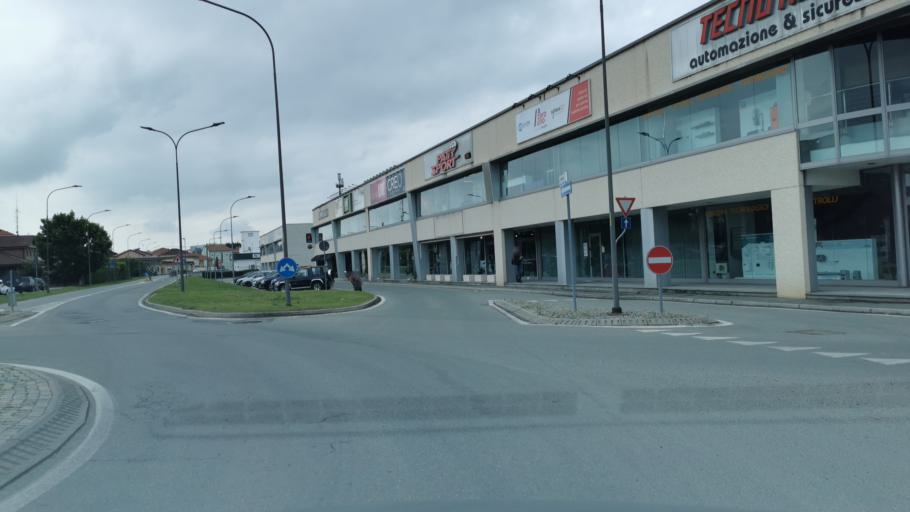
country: IT
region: Piedmont
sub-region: Provincia di Cuneo
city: Savigliano
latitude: 44.6556
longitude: 7.6551
